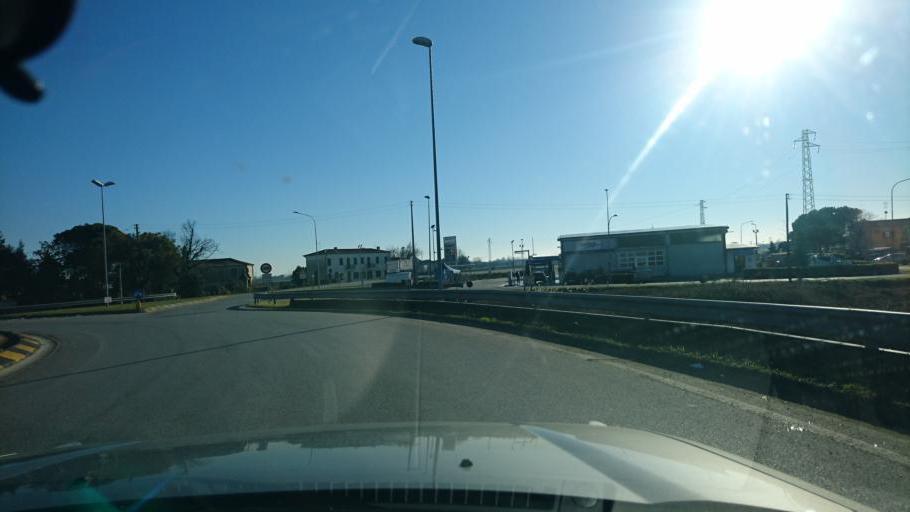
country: IT
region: Veneto
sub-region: Provincia di Rovigo
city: Loreo
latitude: 45.0583
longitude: 12.1964
